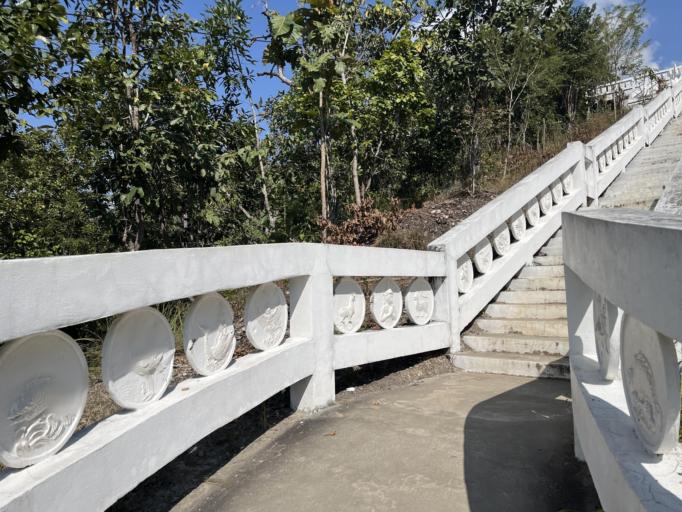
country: TH
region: Mae Hong Son
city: Mae Hi
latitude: 19.3501
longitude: 98.4555
